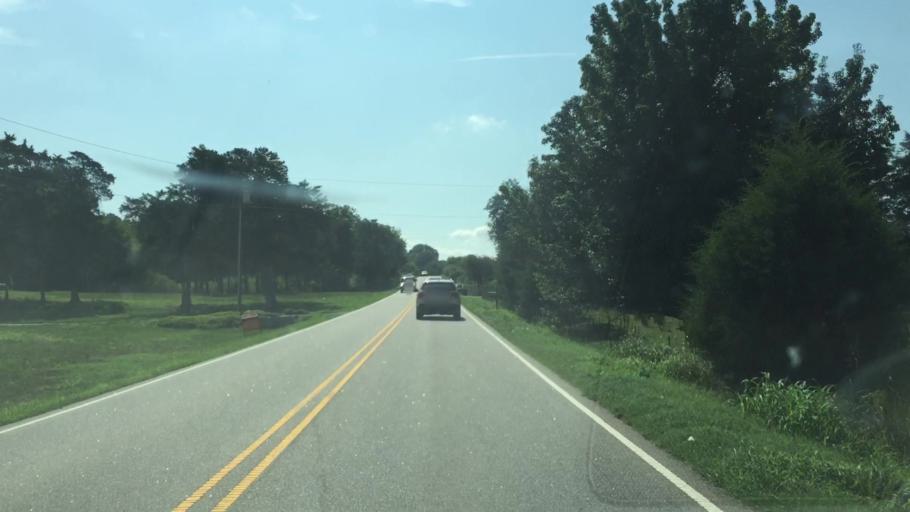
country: US
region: North Carolina
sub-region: Anson County
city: Burnsville
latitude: 35.1063
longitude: -80.3294
